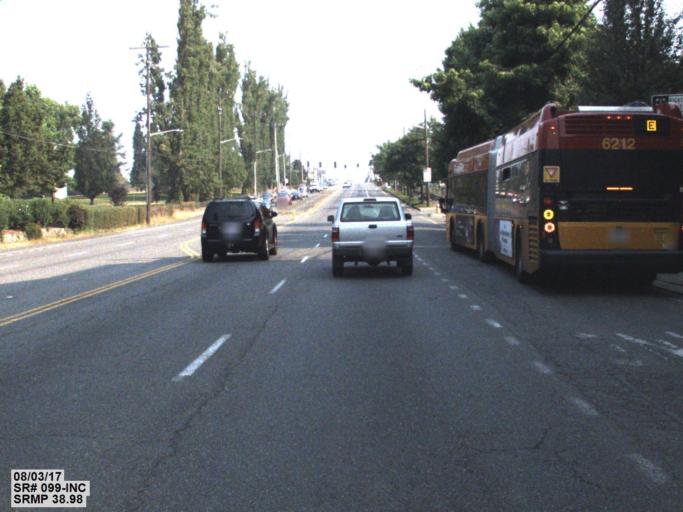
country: US
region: Washington
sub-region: King County
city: Shoreline
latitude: 47.7125
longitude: -122.3448
